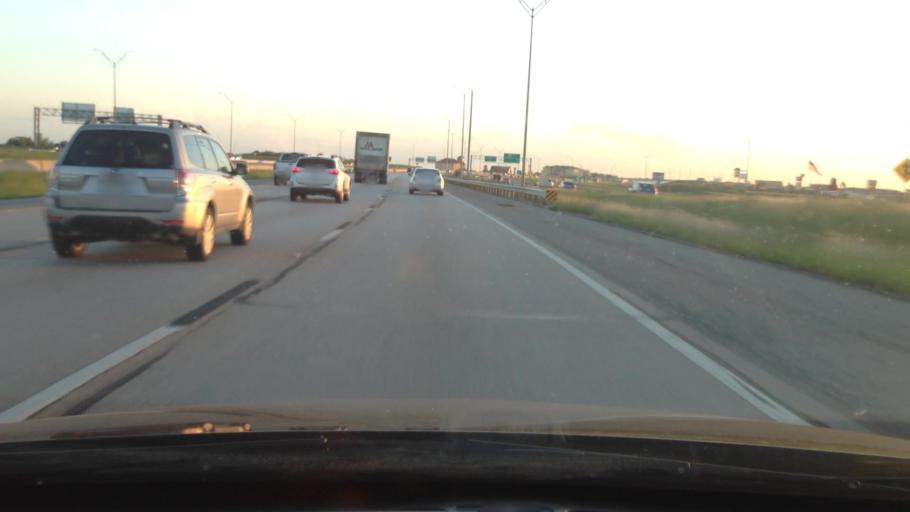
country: US
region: Texas
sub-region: Tarrant County
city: Sansom Park
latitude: 32.8110
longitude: -97.4170
